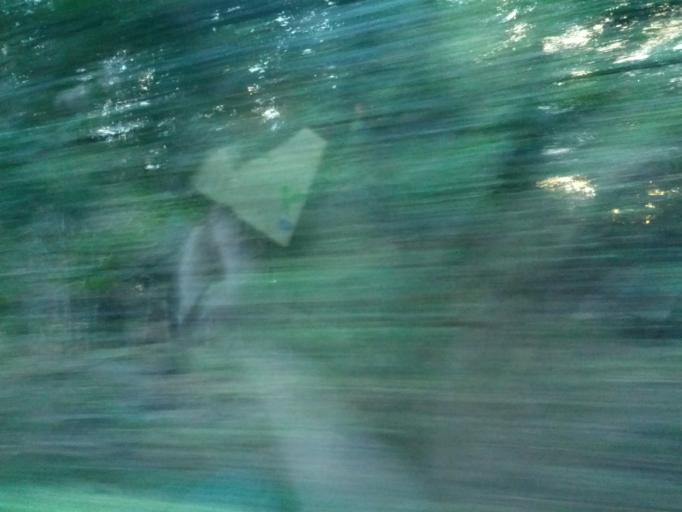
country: IE
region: Connaught
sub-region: County Galway
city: Athenry
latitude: 53.3353
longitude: -8.7027
